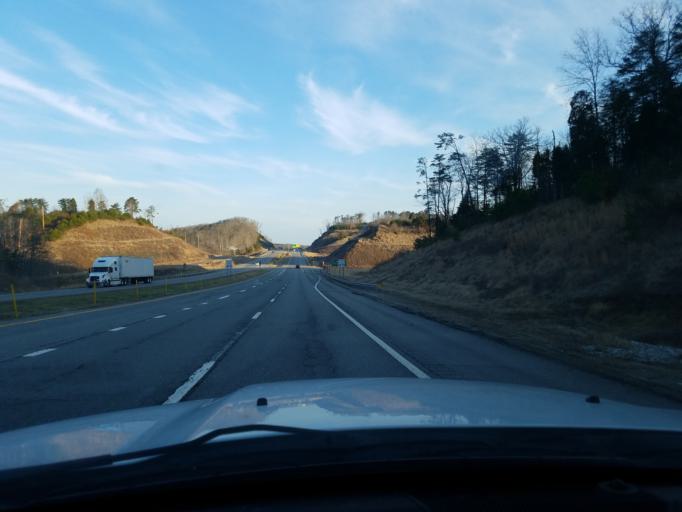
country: US
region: West Virginia
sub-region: Putnam County
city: Buffalo
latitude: 38.5660
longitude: -82.0127
